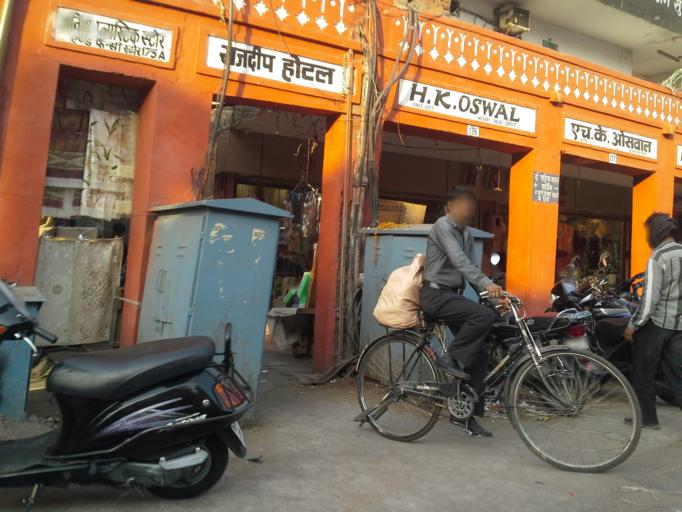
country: IN
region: Rajasthan
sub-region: Jaipur
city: Jaipur
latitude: 26.9165
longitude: 75.8227
